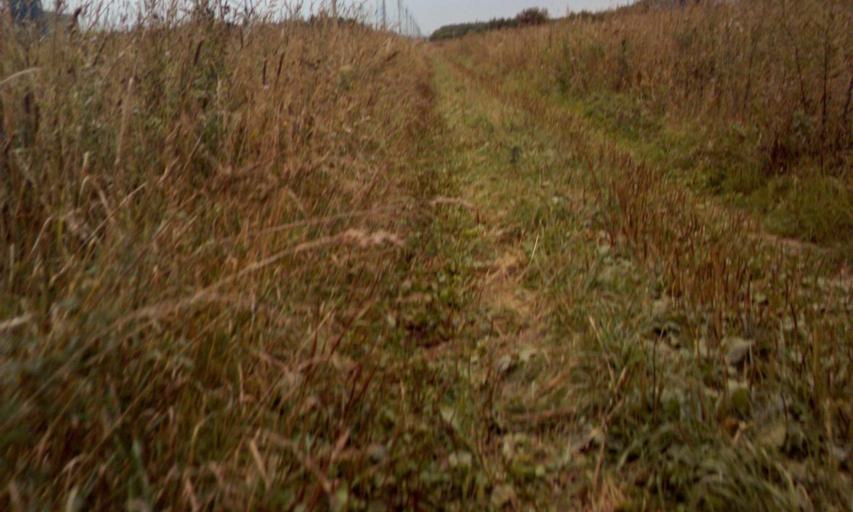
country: RU
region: Moskovskaya
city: Aprelevka
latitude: 55.5814
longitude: 37.1046
